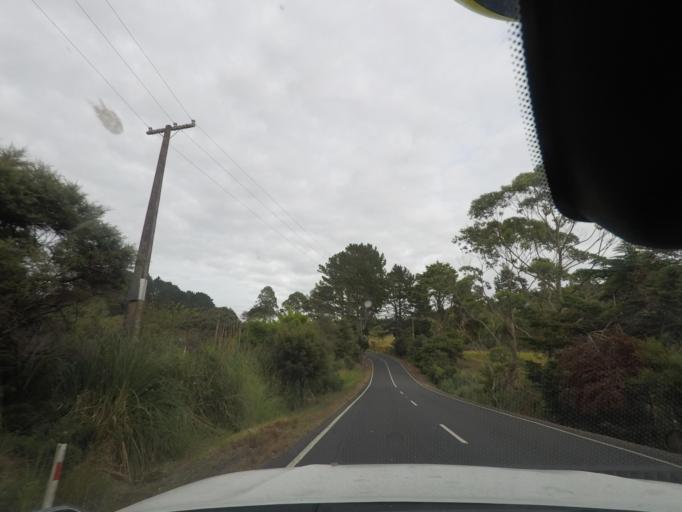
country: NZ
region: Auckland
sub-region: Auckland
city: Parakai
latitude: -36.5214
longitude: 174.2787
